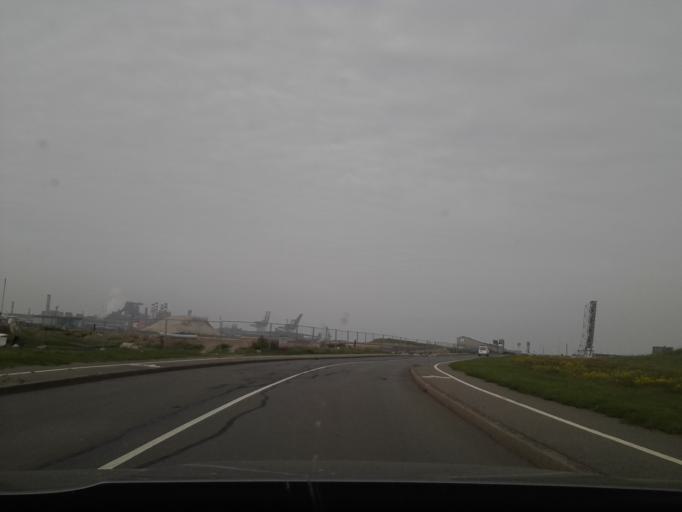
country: FR
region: Nord-Pas-de-Calais
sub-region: Departement du Nord
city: Saint-Pol-sur-Mer
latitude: 51.0516
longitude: 2.3495
